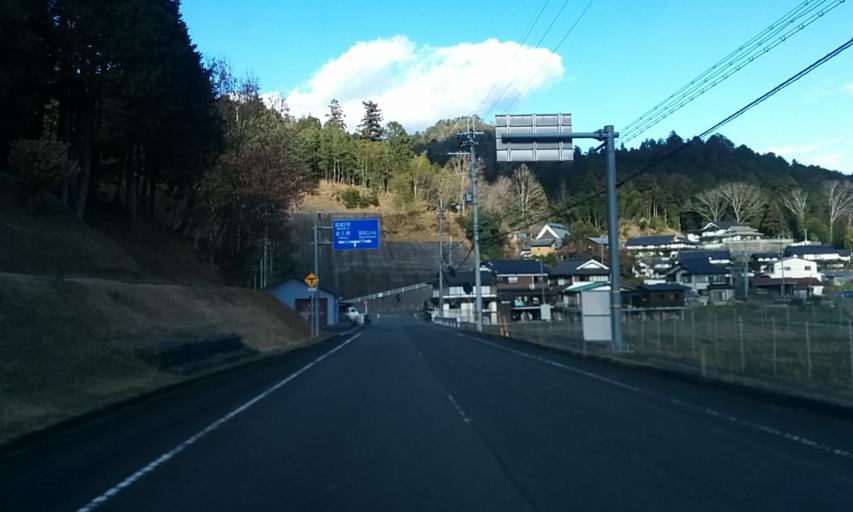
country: JP
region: Kyoto
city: Fukuchiyama
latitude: 35.2816
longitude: 135.0347
